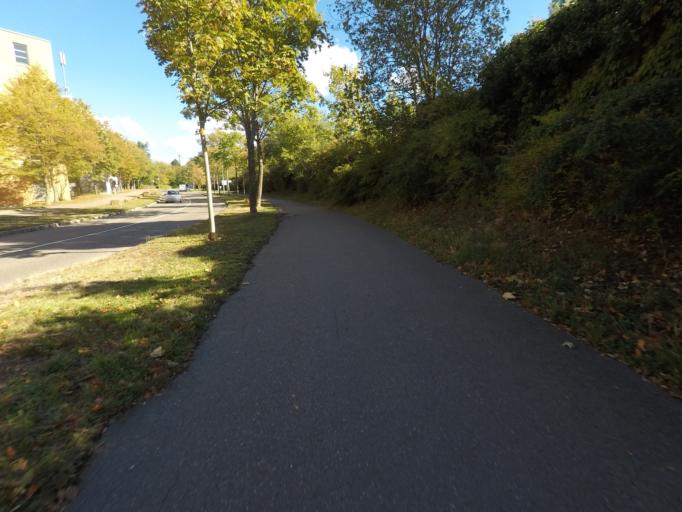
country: DE
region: Baden-Wuerttemberg
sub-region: Regierungsbezirk Stuttgart
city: Gerlingen
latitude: 48.7453
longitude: 9.1092
